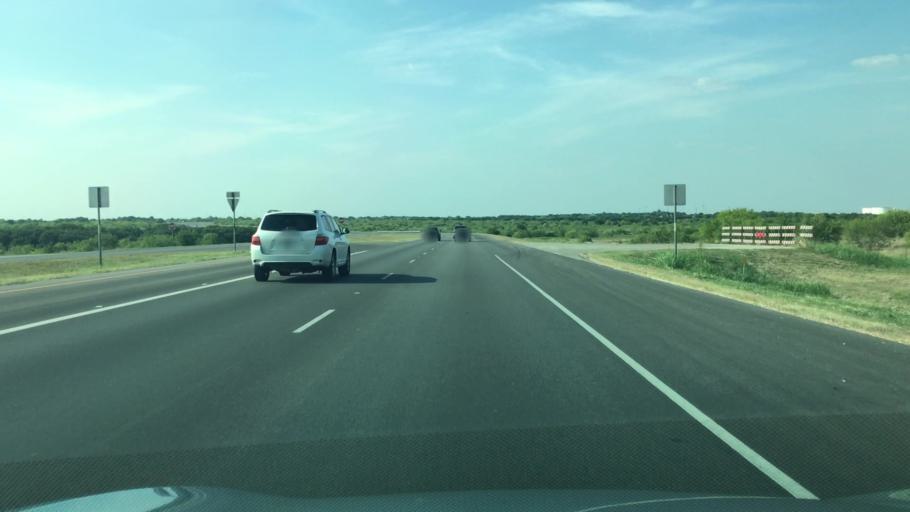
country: US
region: Texas
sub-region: Hays County
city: Kyle
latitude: 30.0341
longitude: -97.8722
